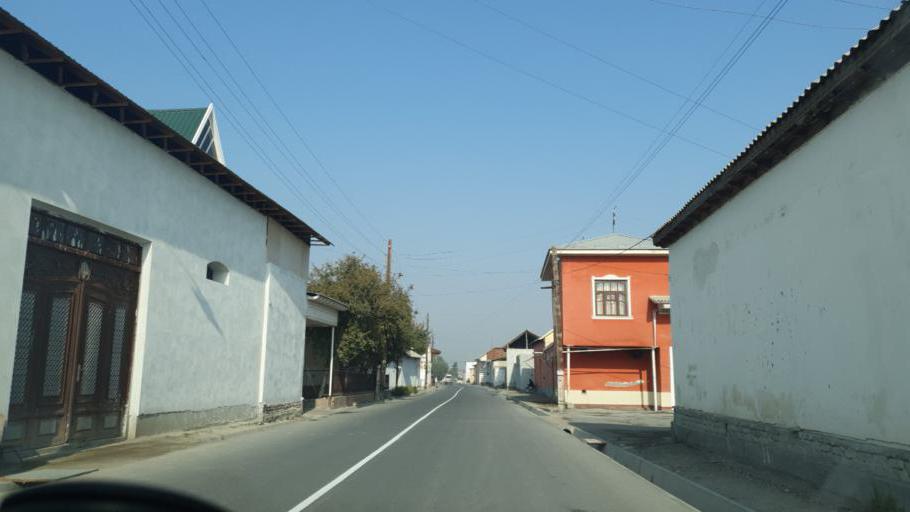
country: UZ
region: Fergana
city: Qo`qon
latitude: 40.5849
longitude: 70.9075
